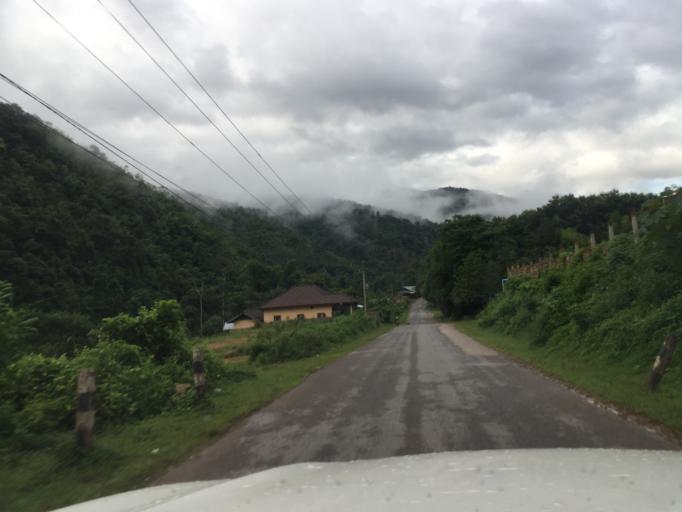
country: LA
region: Oudomxai
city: Muang La
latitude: 20.8744
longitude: 102.1346
